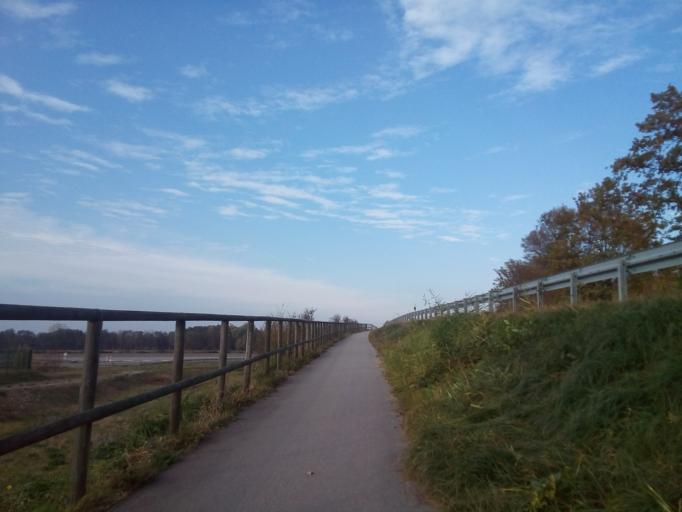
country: DE
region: Baden-Wuerttemberg
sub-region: Karlsruhe Region
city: Zell
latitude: 48.6749
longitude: 8.0570
